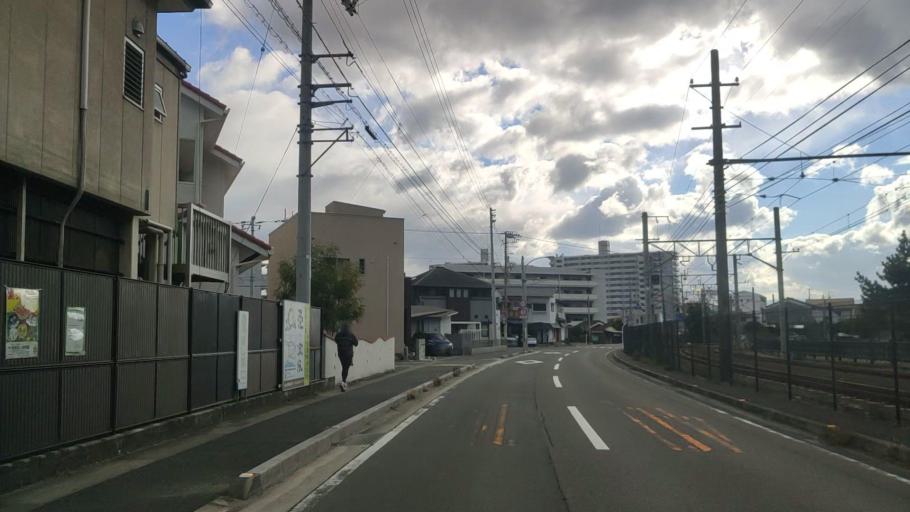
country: JP
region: Ehime
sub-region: Shikoku-chuo Shi
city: Matsuyama
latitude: 33.8692
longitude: 132.7167
